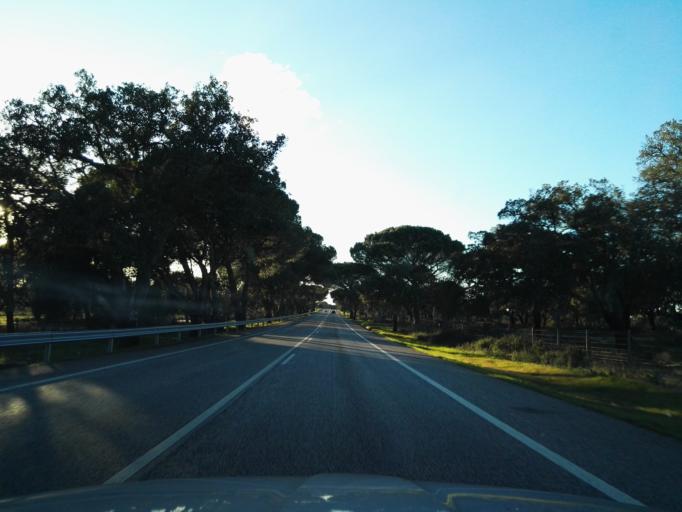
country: PT
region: Santarem
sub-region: Benavente
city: Poceirao
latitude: 38.8456
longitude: -8.7537
